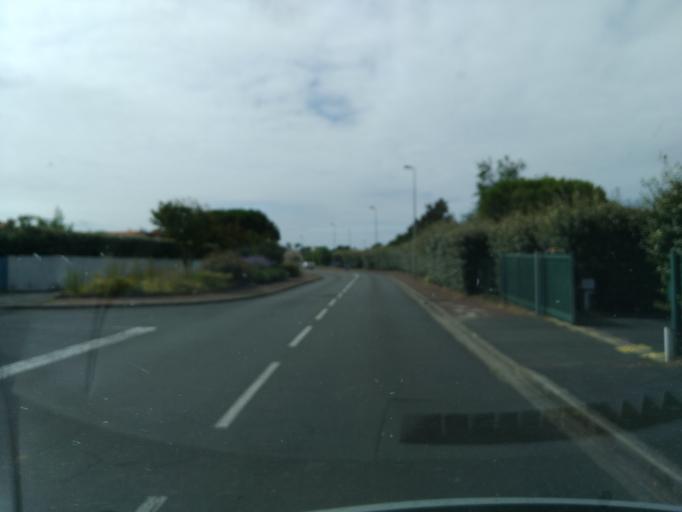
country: FR
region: Poitou-Charentes
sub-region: Departement de la Charente-Maritime
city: Saint-Palais-sur-Mer
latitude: 45.6528
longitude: -1.0846
